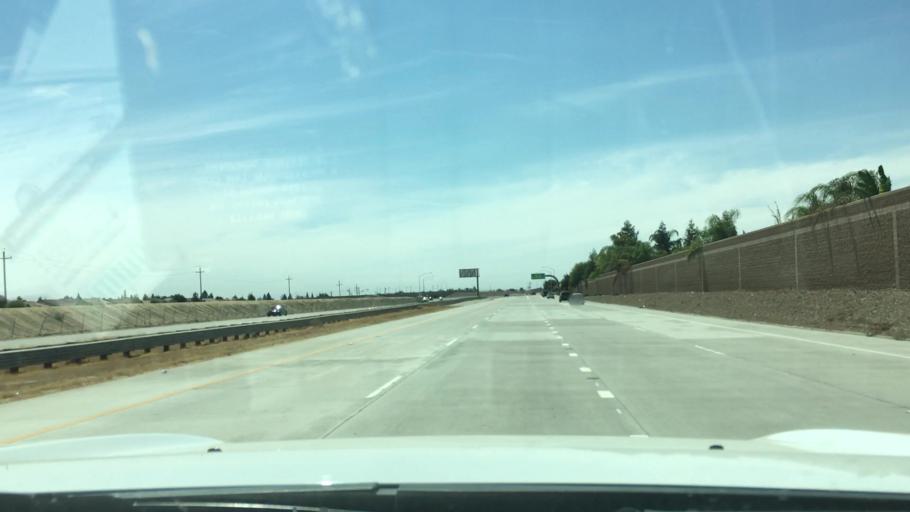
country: US
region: California
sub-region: Kern County
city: Rosedale
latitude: 35.3621
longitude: -119.1355
